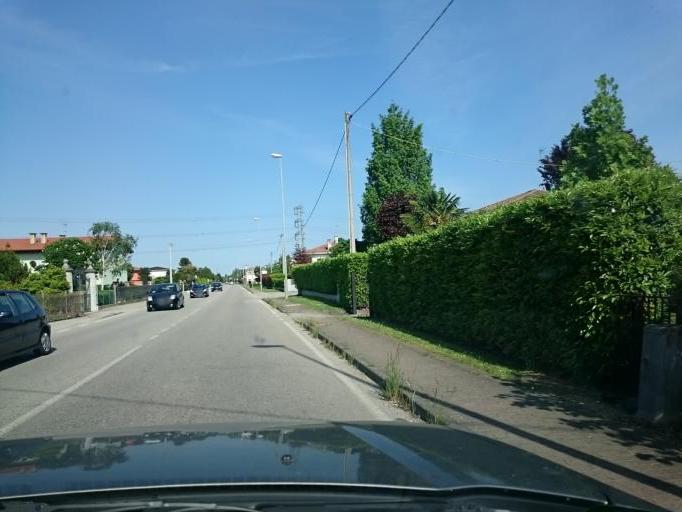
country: IT
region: Veneto
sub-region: Provincia di Venezia
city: Sambruson
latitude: 45.4140
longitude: 12.1105
